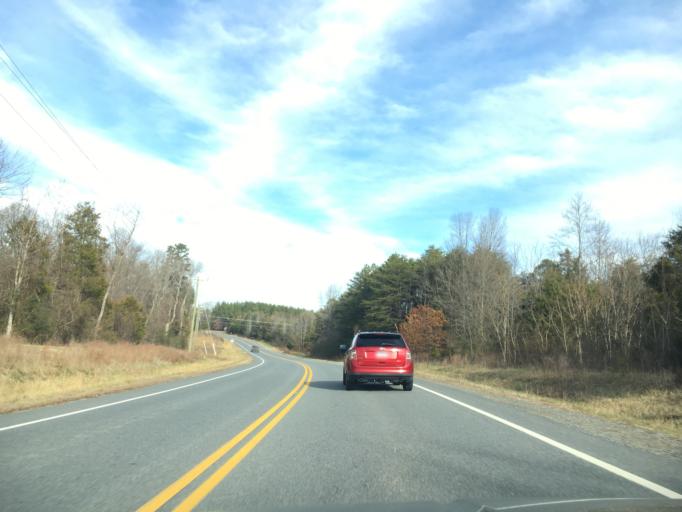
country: US
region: Virginia
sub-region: Louisa County
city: Louisa
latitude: 38.0461
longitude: -77.8807
